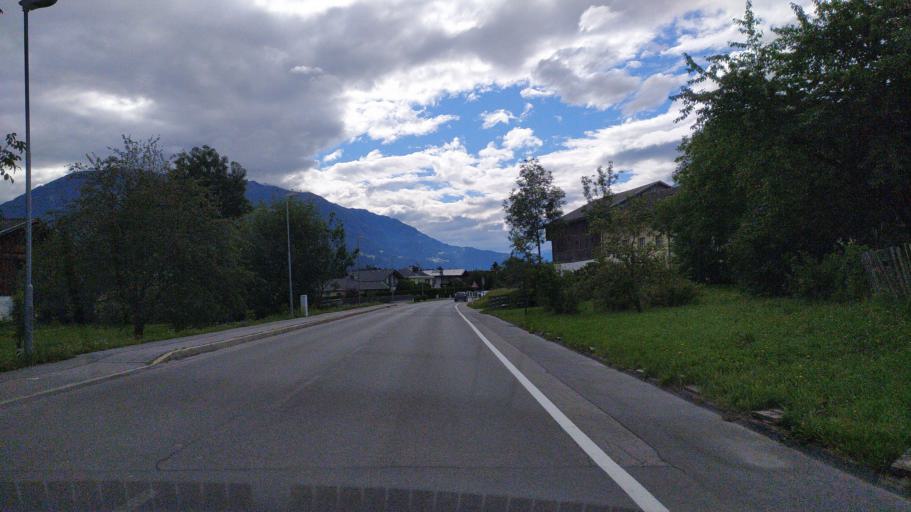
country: AT
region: Tyrol
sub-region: Politischer Bezirk Lienz
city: Tristach
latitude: 46.8193
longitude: 12.7915
